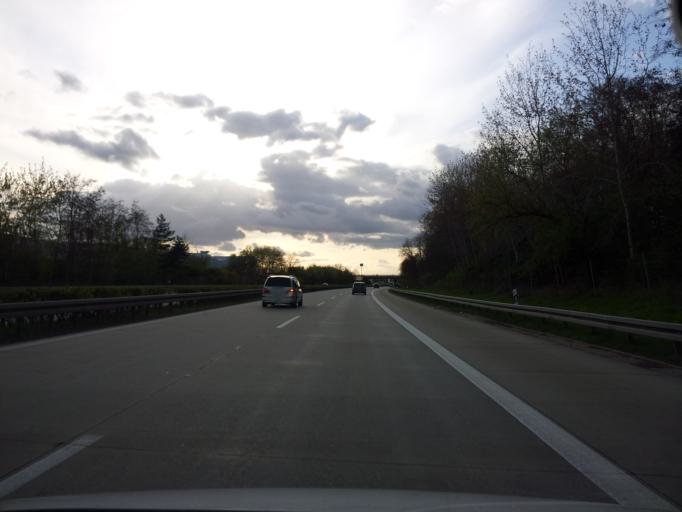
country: DE
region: Brandenburg
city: Cottbus
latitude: 51.7189
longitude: 14.3251
